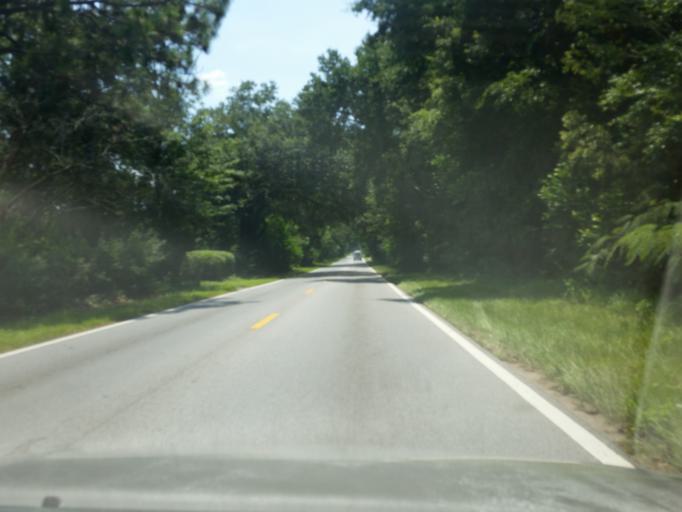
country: US
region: Florida
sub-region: Escambia County
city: Ensley
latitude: 30.4961
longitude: -87.2713
